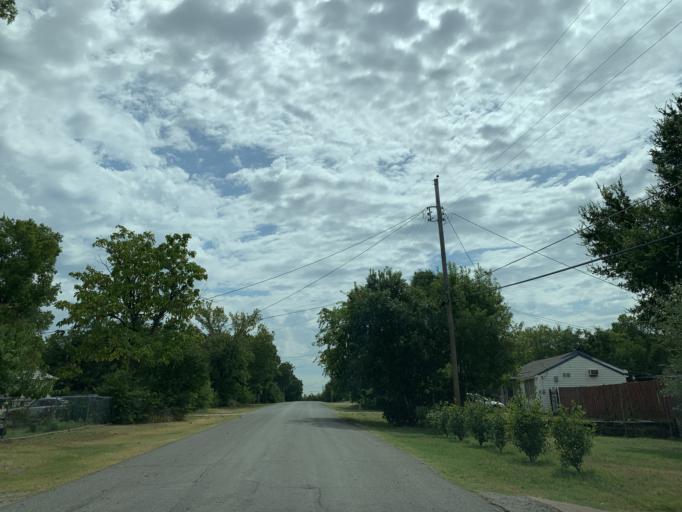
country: US
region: Texas
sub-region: Dallas County
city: Duncanville
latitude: 32.6712
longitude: -96.8340
